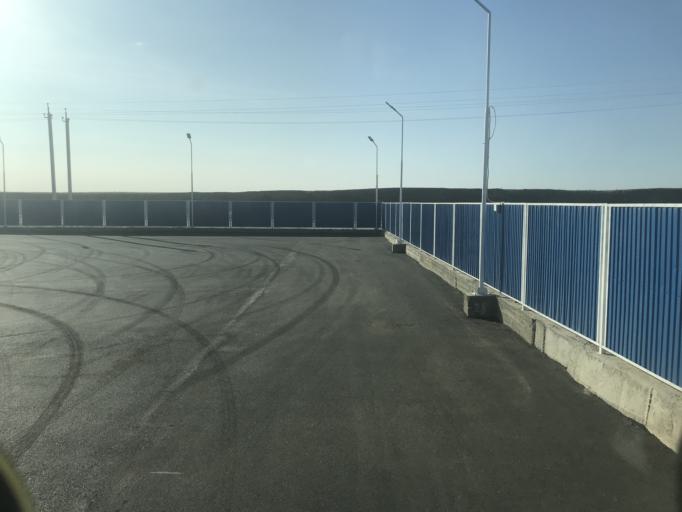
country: KZ
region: Ongtustik Qazaqstan
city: Temirlanovka
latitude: 42.5718
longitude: 69.3112
